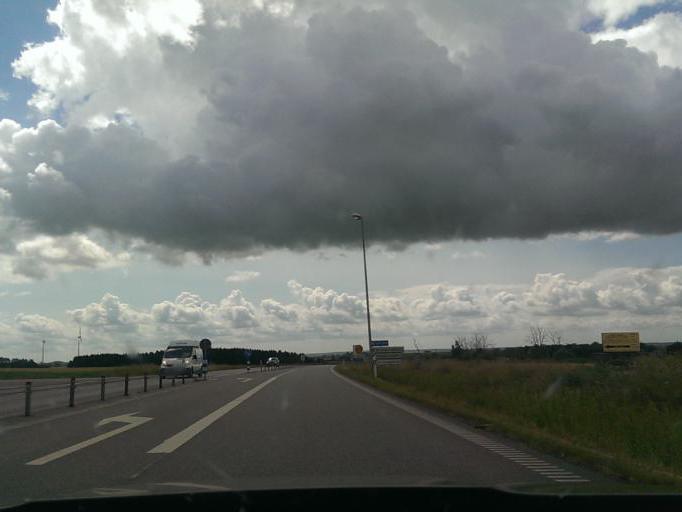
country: SE
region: Skane
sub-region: Eslovs Kommun
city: Eslov
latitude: 55.8249
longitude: 13.3351
